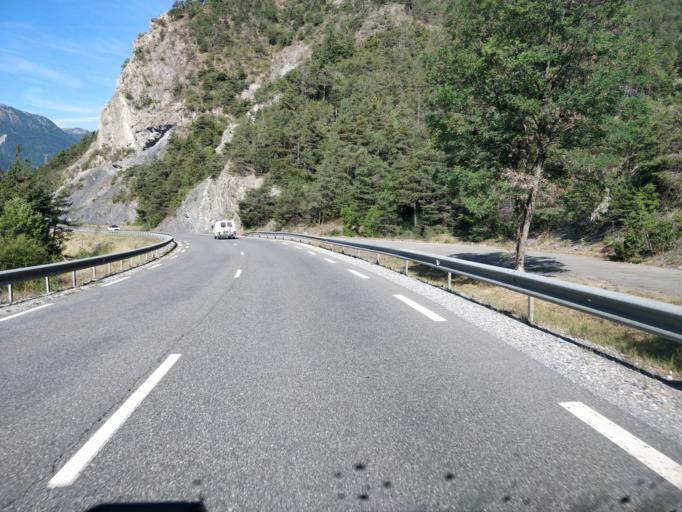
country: FR
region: Provence-Alpes-Cote d'Azur
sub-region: Departement des Alpes-de-Haute-Provence
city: Barcelonnette
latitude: 44.4014
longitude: 6.5276
